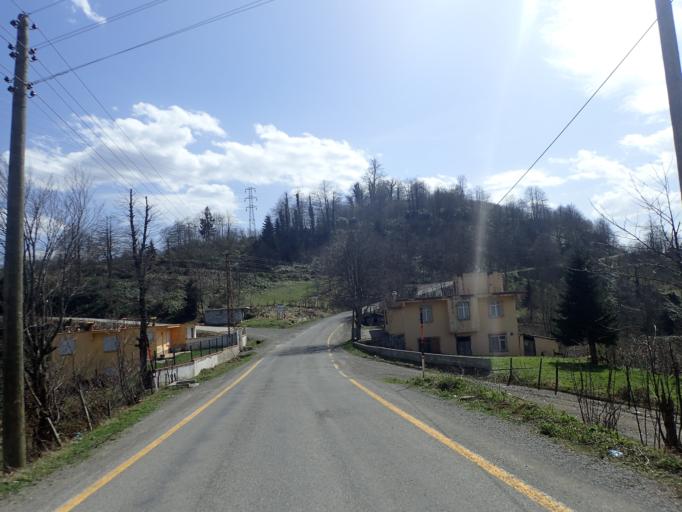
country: TR
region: Ordu
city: Kabaduz
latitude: 40.8171
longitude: 37.9067
